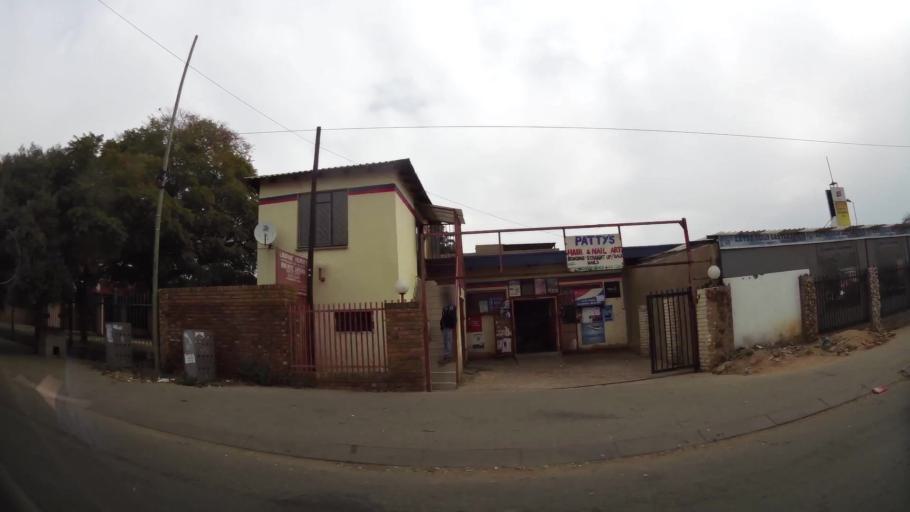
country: ZA
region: Gauteng
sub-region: City of Tshwane Metropolitan Municipality
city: Pretoria
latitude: -25.7113
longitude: 28.3486
